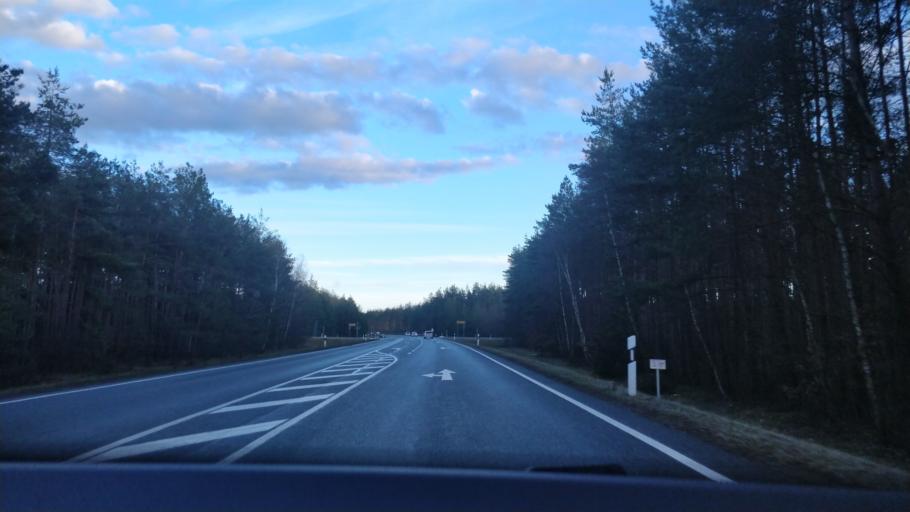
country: DE
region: Bavaria
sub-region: Upper Palatinate
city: Schwarzenbach
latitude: 49.7263
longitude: 11.9658
